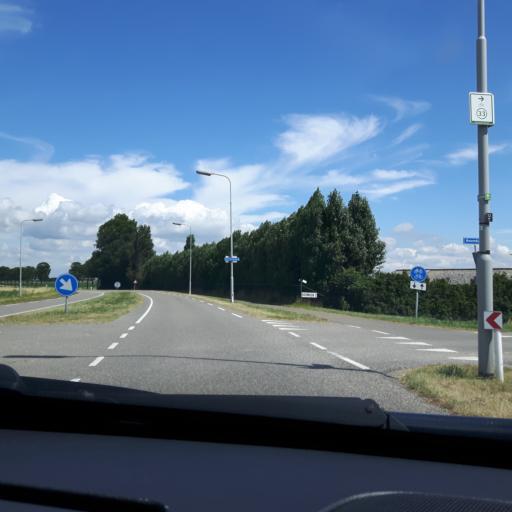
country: NL
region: Zeeland
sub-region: Gemeente Goes
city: Goes
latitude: 51.5627
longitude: 3.8619
